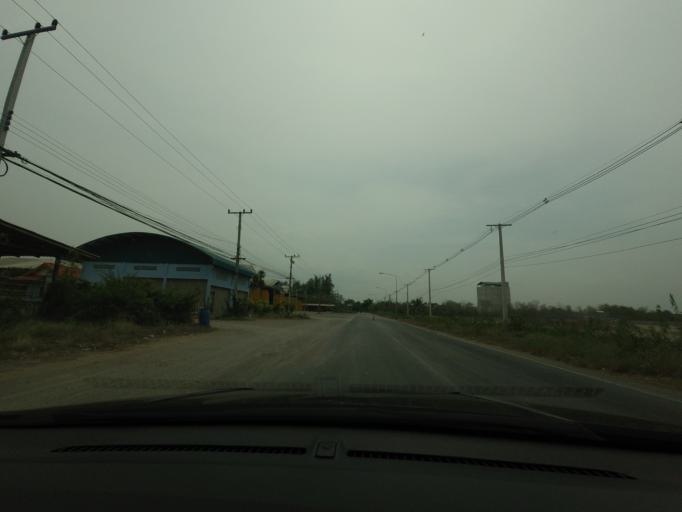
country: TH
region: Phetchaburi
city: Ban Laem
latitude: 13.2058
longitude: 99.9677
